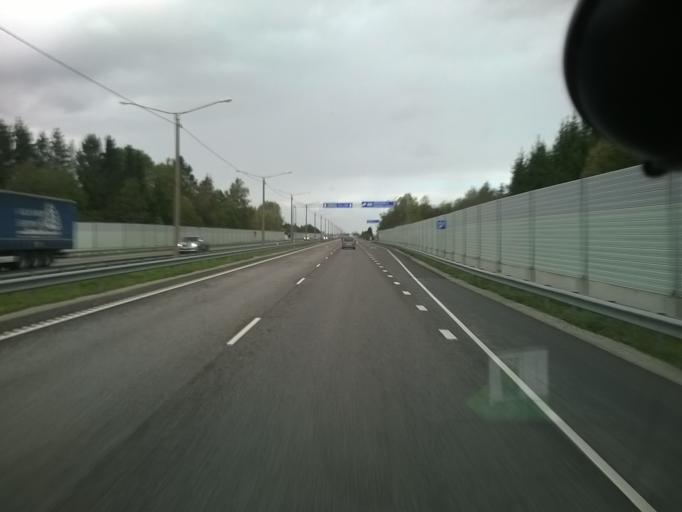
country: EE
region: Harju
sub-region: Rae vald
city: Jueri
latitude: 59.3735
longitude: 24.8514
